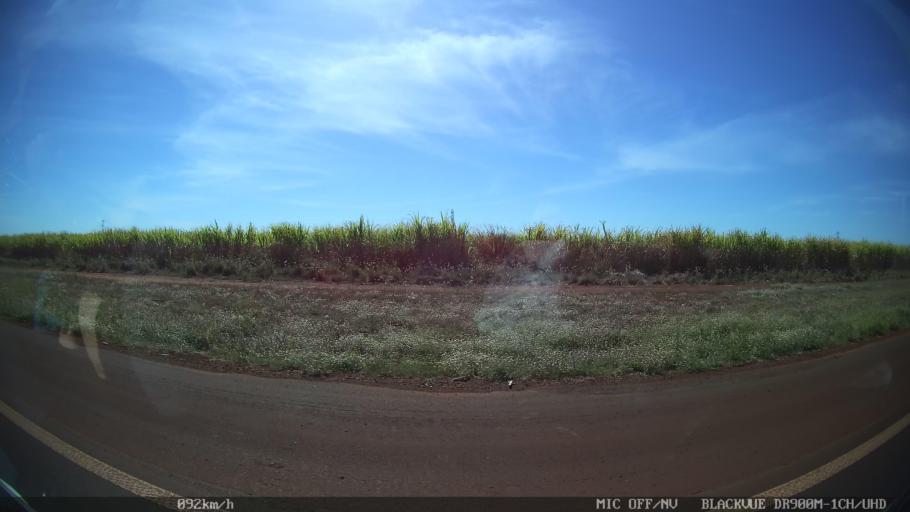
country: BR
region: Sao Paulo
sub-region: Guaira
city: Guaira
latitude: -20.4446
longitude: -48.2664
